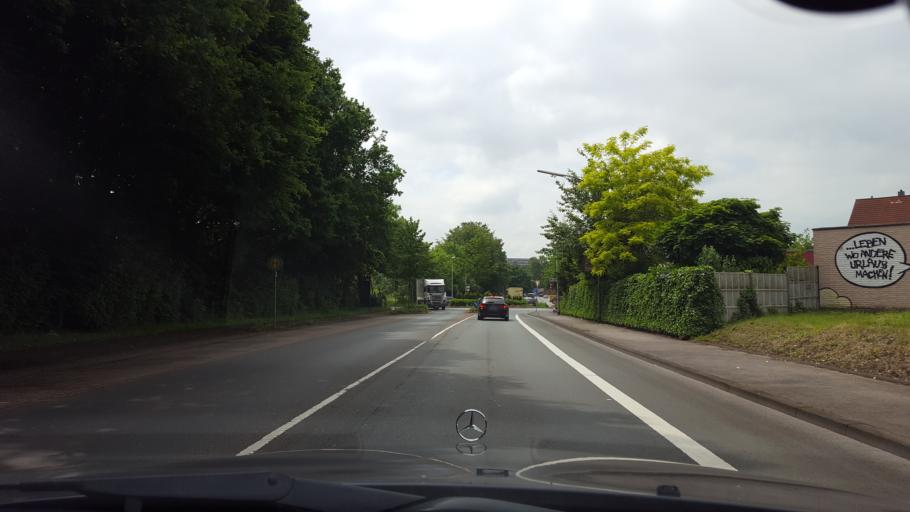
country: DE
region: North Rhine-Westphalia
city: Witten
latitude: 51.4526
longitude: 7.3506
